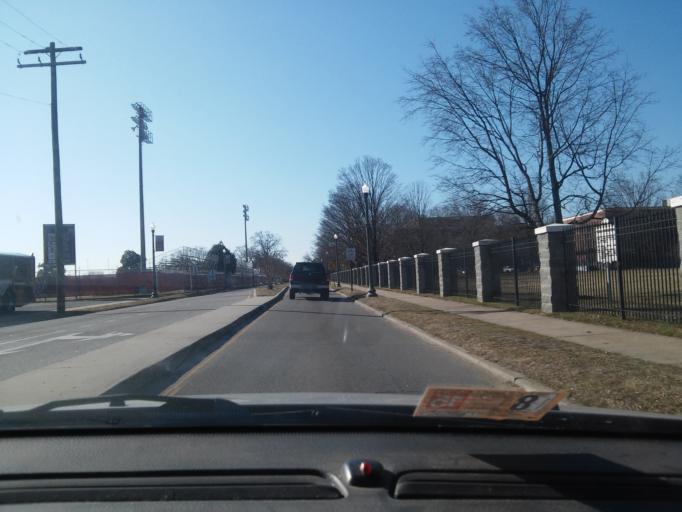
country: US
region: Virginia
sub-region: City of Richmond
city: Richmond
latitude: 37.5624
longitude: -77.4485
